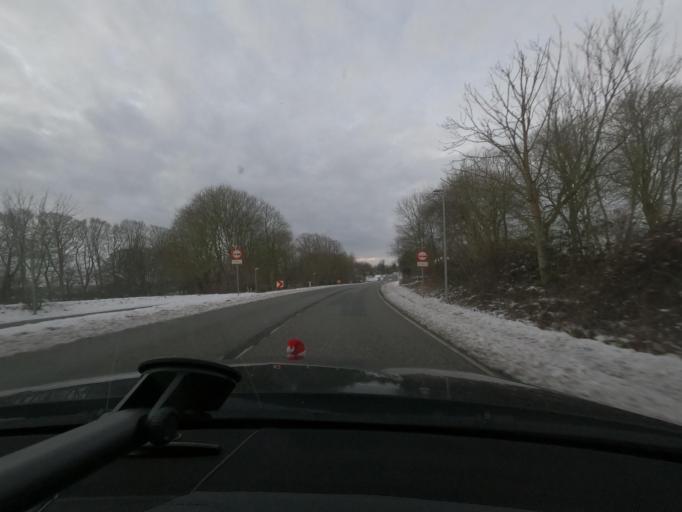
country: DK
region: South Denmark
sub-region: Sonderborg Kommune
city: Grasten
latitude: 54.9054
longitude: 9.5758
